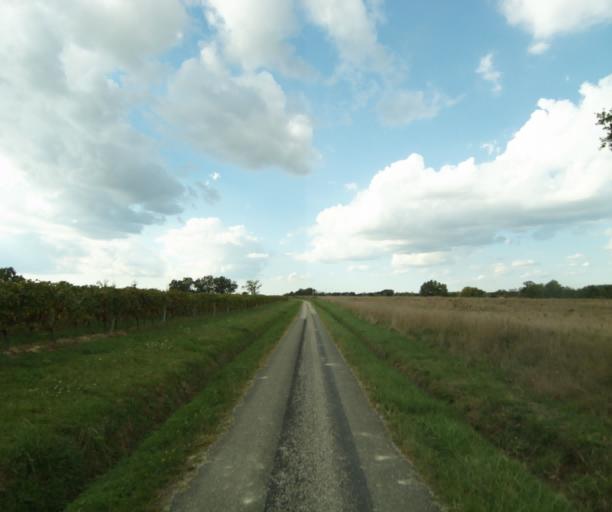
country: FR
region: Midi-Pyrenees
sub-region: Departement du Gers
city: Cazaubon
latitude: 43.9002
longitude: -0.1059
